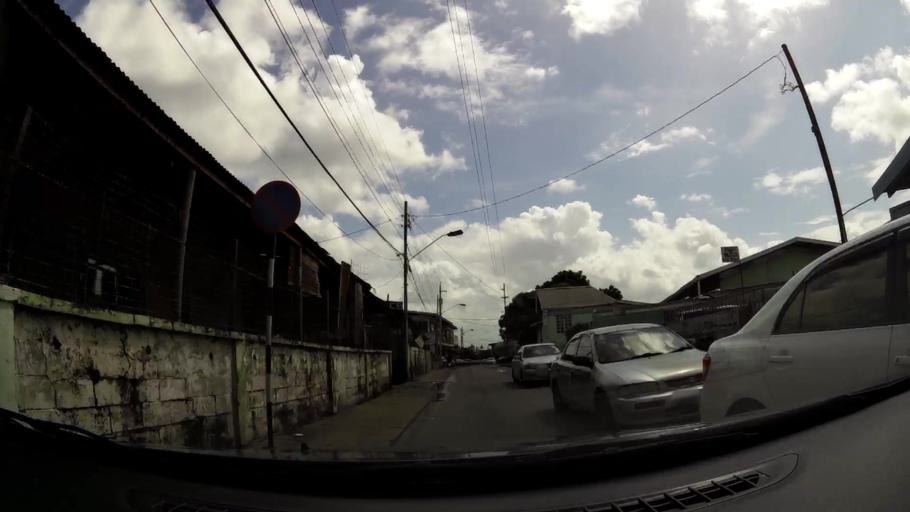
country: TT
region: Borough of Arima
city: Arima
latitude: 10.6407
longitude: -61.2801
